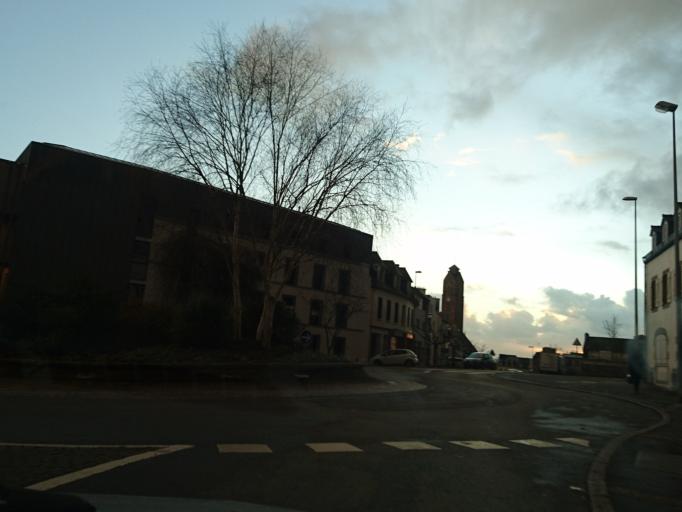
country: FR
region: Brittany
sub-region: Departement du Finistere
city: Guipavas
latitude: 48.4358
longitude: -4.3994
